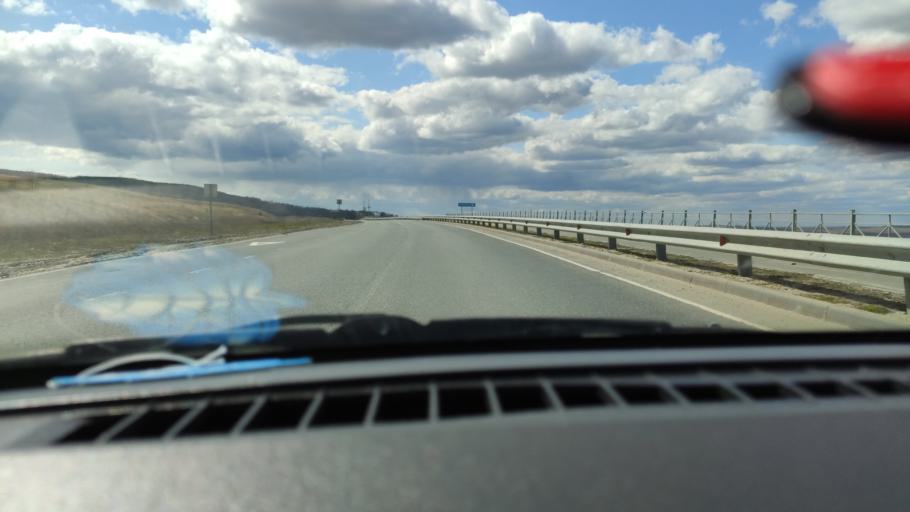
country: RU
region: Saratov
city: Alekseyevka
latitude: 52.3422
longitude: 47.9354
